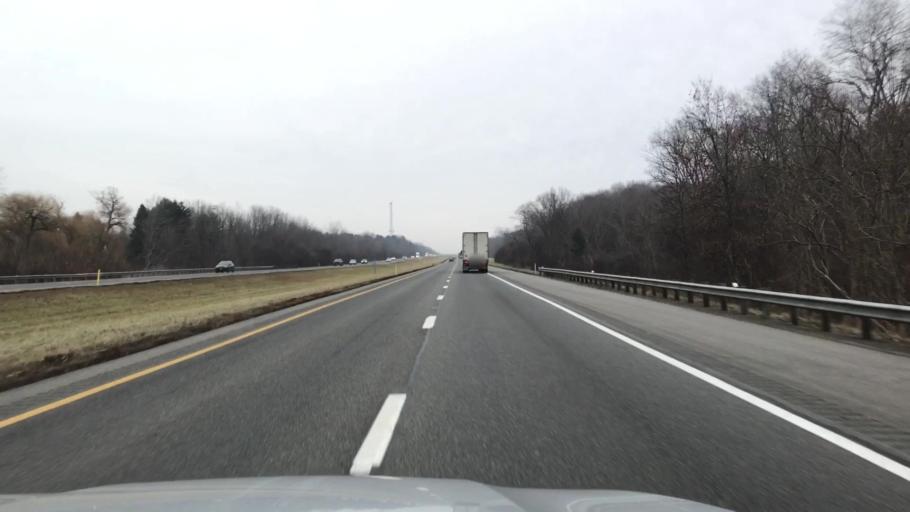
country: US
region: Ohio
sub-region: Lake County
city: Madison
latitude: 41.7410
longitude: -81.0924
